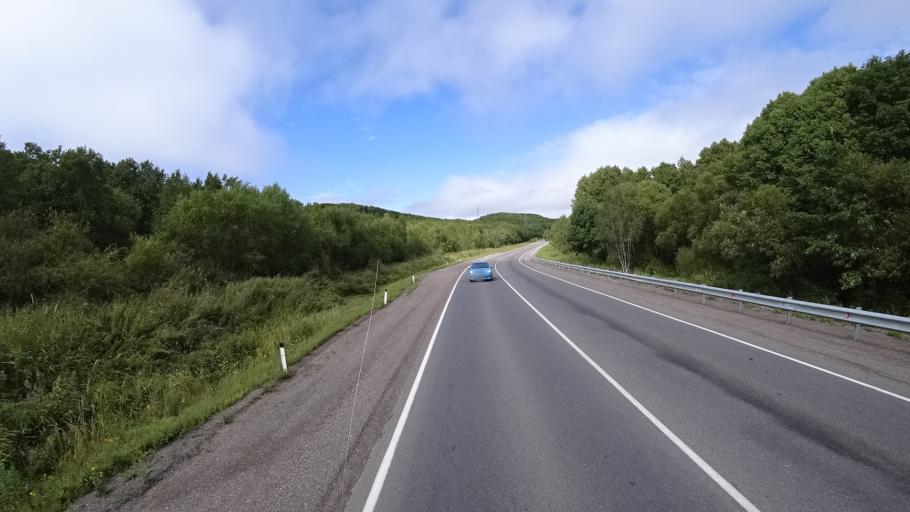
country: RU
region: Primorskiy
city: Lyalichi
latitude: 44.1162
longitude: 132.4191
